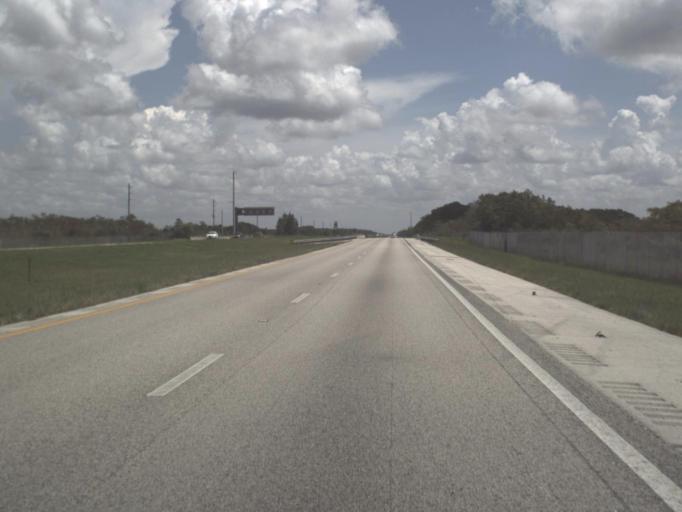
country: US
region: Florida
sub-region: Collier County
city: Immokalee
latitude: 26.1689
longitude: -81.0462
